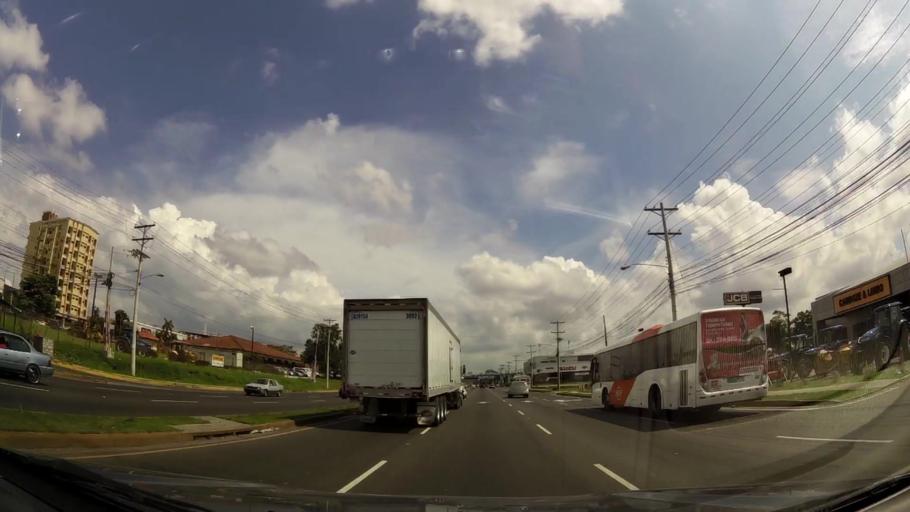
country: PA
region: Panama
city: San Miguelito
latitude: 9.0362
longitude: -79.4828
